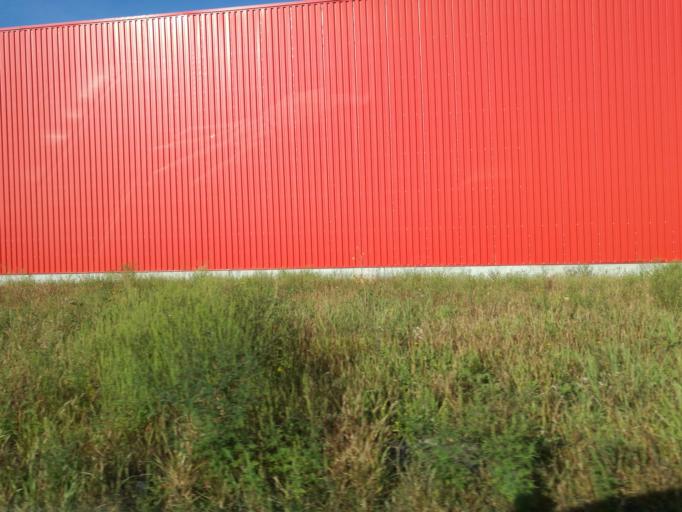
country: RO
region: Bihor
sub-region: Comuna Biharea
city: Oradea
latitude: 47.0442
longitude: 21.9068
